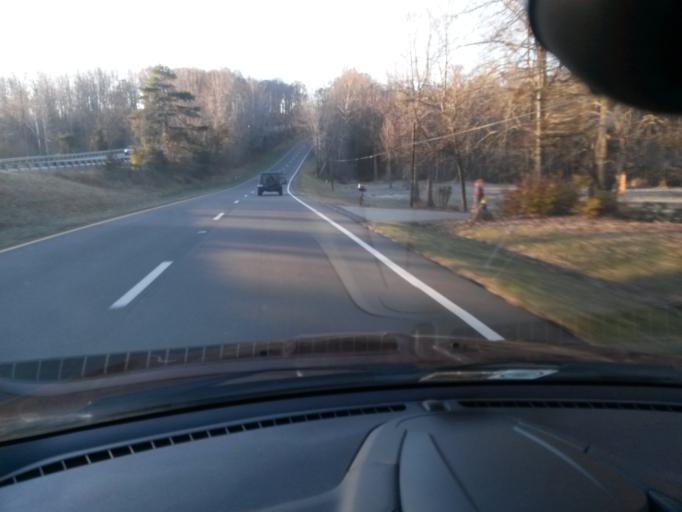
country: US
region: Virginia
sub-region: Franklin County
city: Henry Fork
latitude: 36.9154
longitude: -79.8649
